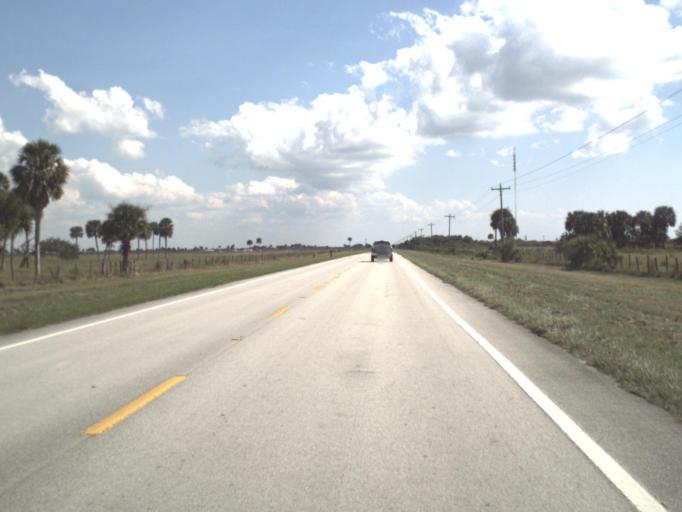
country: US
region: Florida
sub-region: Okeechobee County
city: Okeechobee
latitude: 27.3536
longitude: -80.9565
